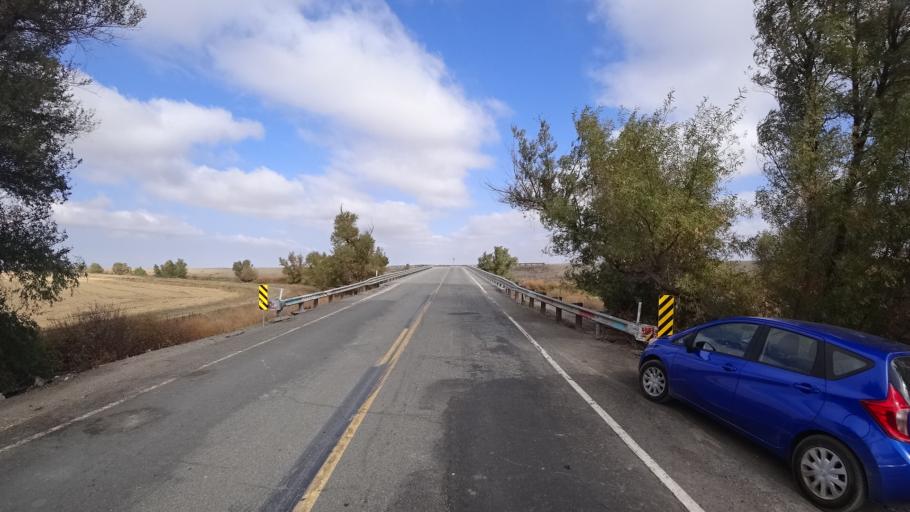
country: US
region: California
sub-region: Yolo County
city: Woodland
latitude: 38.8115
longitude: -121.7743
